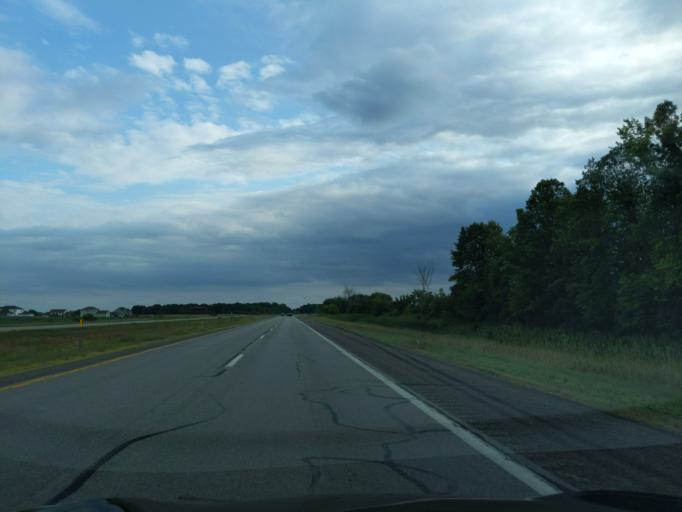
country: US
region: Michigan
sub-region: Isabella County
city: Mount Pleasant
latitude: 43.6591
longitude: -84.7589
